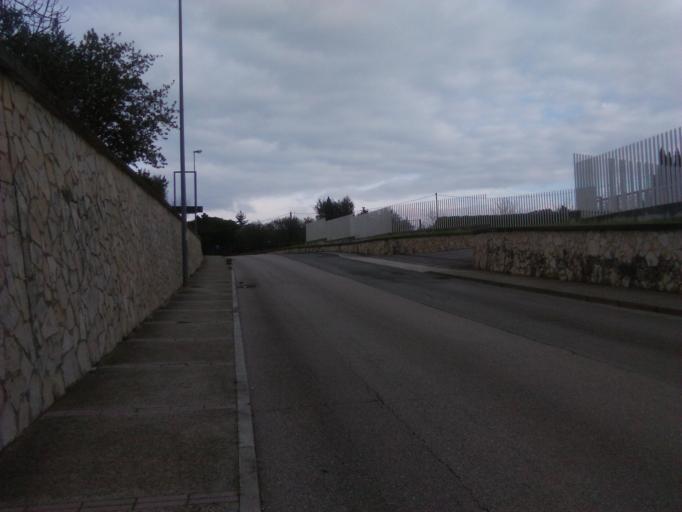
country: IT
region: Umbria
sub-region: Provincia di Perugia
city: Perugia
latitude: 43.0919
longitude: 12.3641
